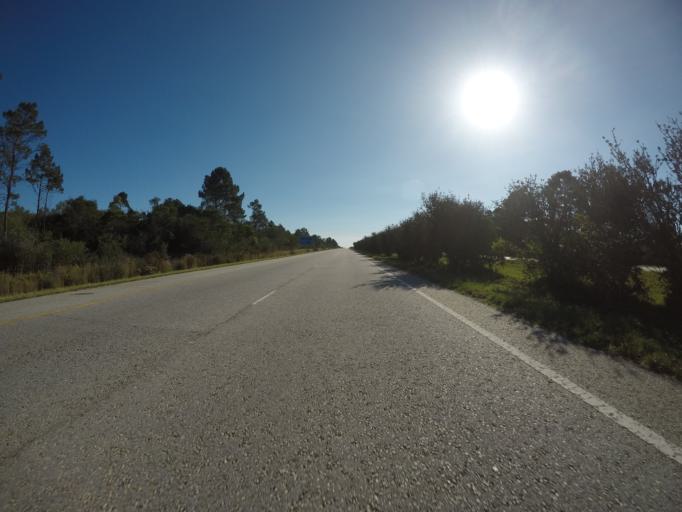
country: ZA
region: Eastern Cape
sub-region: Nelson Mandela Bay Metropolitan Municipality
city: Uitenhage
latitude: -33.9269
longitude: 25.3266
